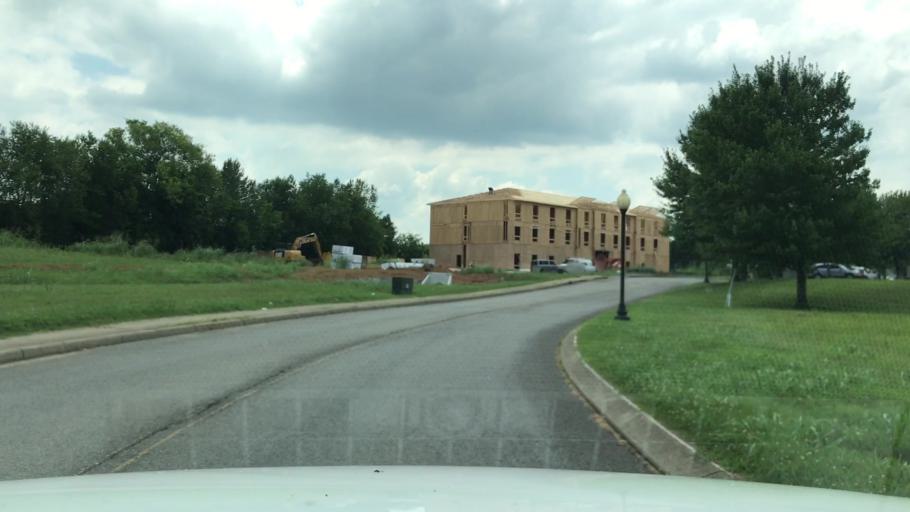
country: US
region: Tennessee
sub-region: Sumner County
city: Gallatin
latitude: 36.3807
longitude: -86.4715
